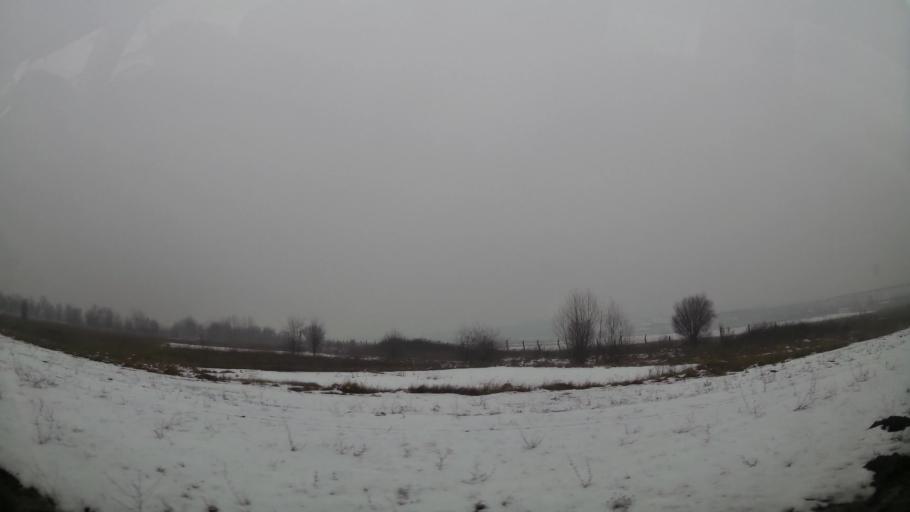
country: MK
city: Miladinovci
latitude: 41.9625
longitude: 21.6296
